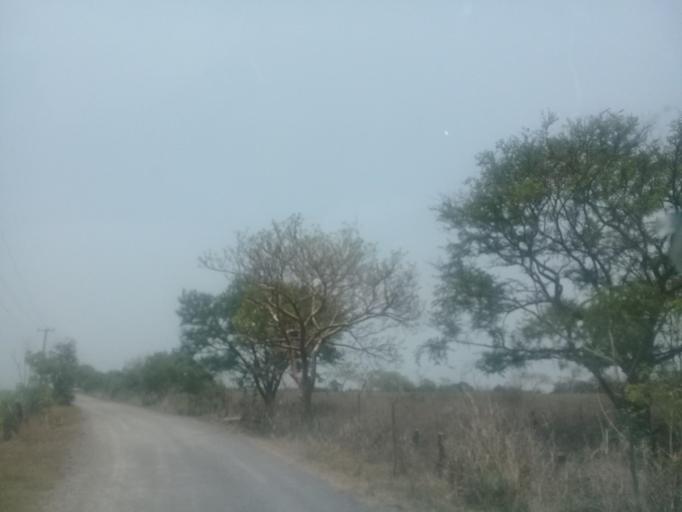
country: MX
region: Veracruz
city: Jamapa
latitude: 19.0979
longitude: -96.2356
